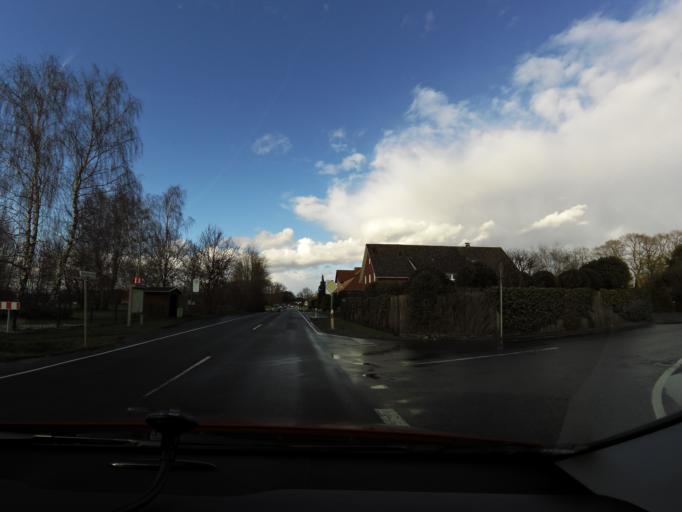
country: DE
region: North Rhine-Westphalia
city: Rietberg
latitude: 51.8660
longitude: 8.4501
